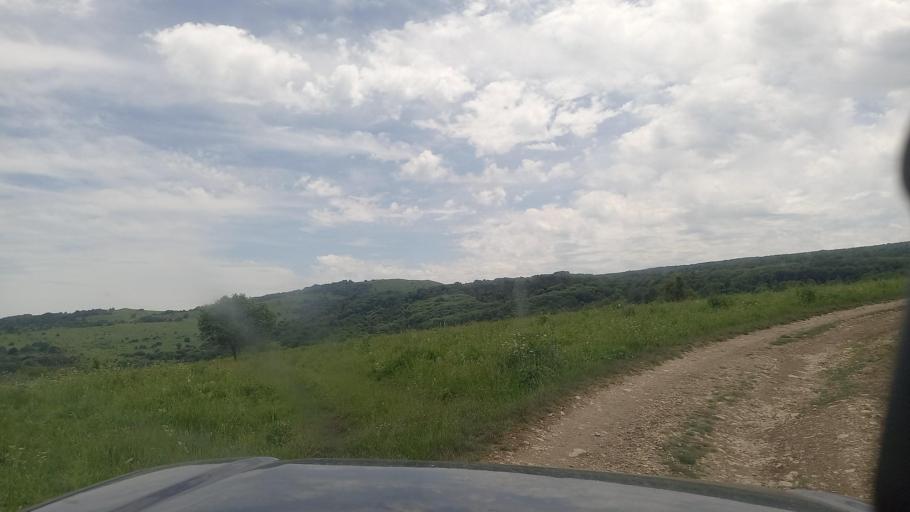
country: RU
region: Karachayevo-Cherkesiya
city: Pregradnaya
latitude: 44.0887
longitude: 41.1922
